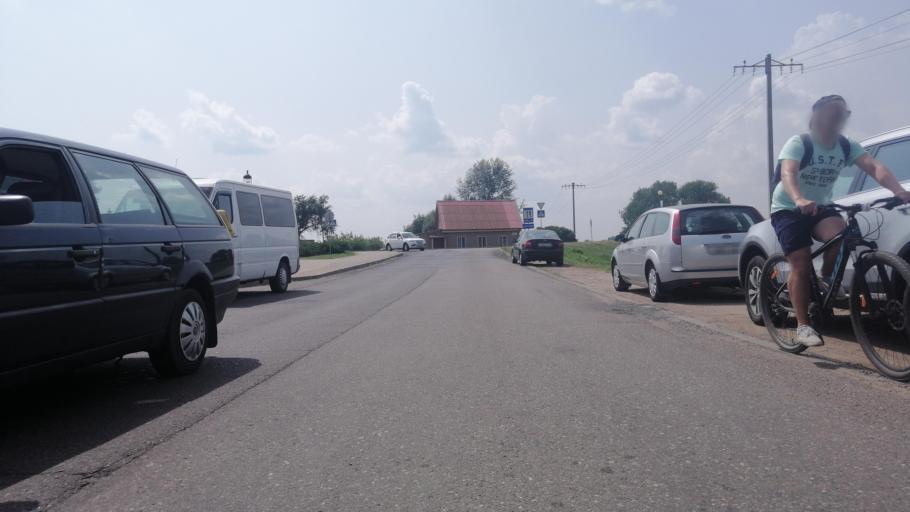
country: BY
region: Grodnenskaya
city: Mir
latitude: 53.4519
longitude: 26.4699
